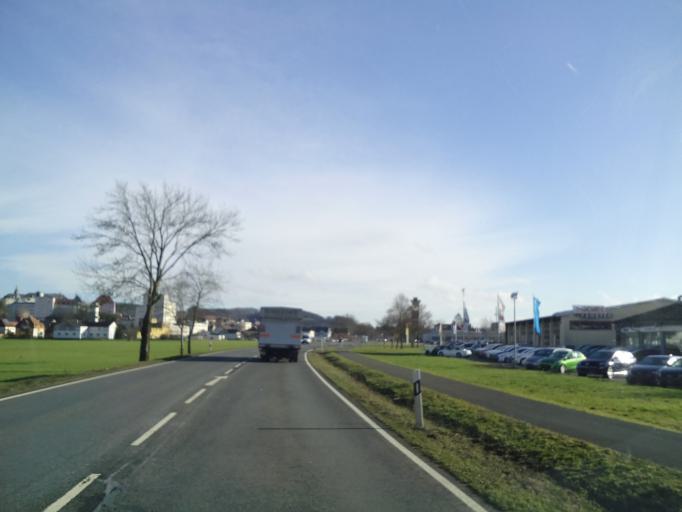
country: DE
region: Bavaria
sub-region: Upper Franconia
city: Burgkunstadt
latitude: 50.1426
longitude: 11.2396
